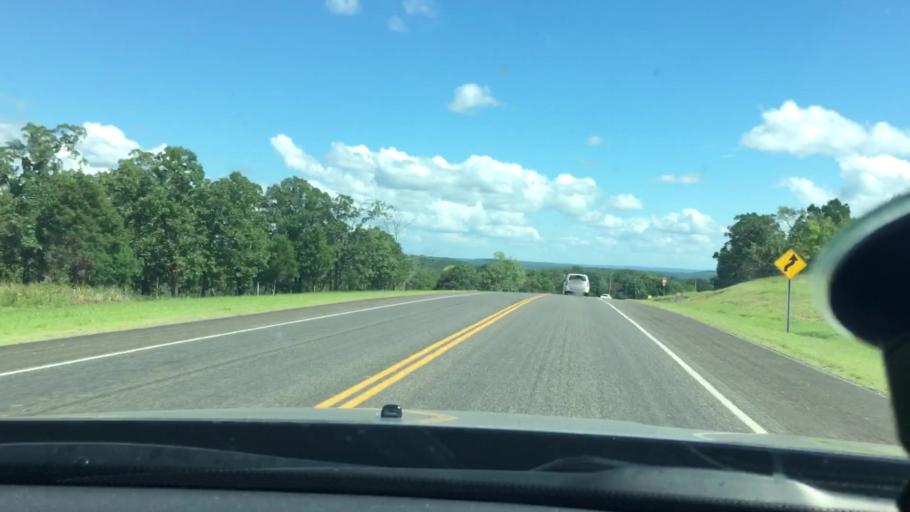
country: US
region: Oklahoma
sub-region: Sequoyah County
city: Vian
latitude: 35.5524
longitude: -94.9728
